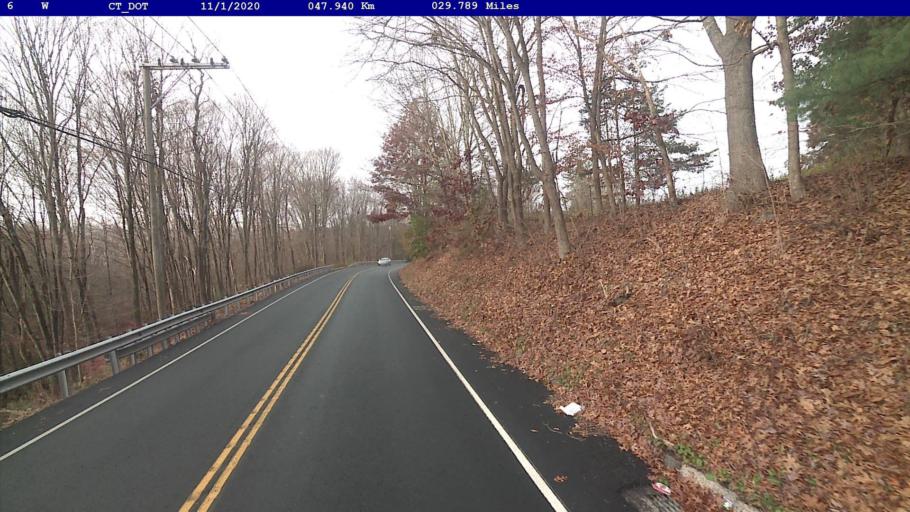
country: US
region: Connecticut
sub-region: Litchfield County
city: Woodbury Center
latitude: 41.5746
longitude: -73.1827
